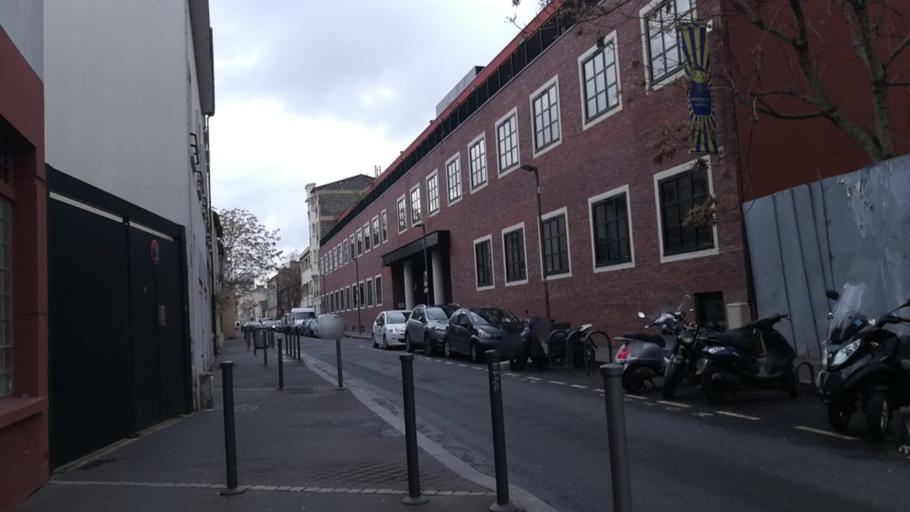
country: FR
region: Ile-de-France
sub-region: Paris
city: Saint-Ouen
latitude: 48.9057
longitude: 2.3364
